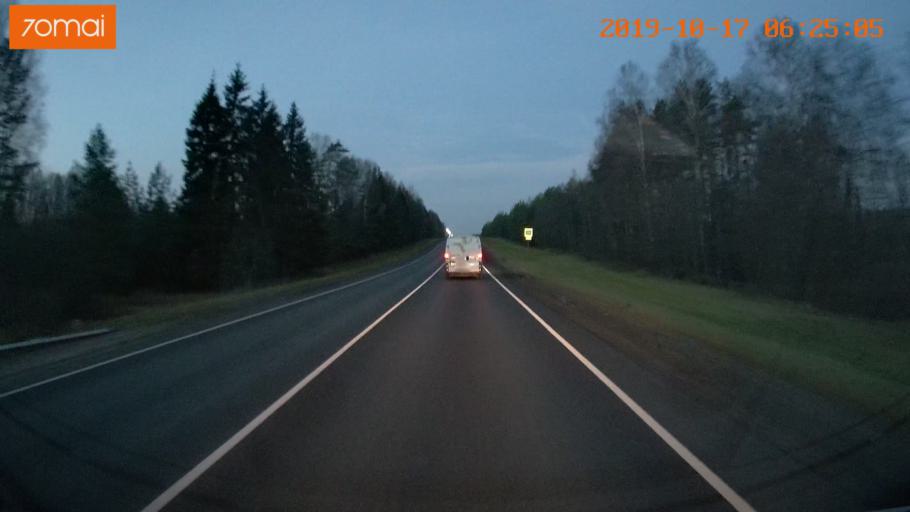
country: RU
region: Ivanovo
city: Lezhnevo
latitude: 56.7711
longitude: 40.8143
